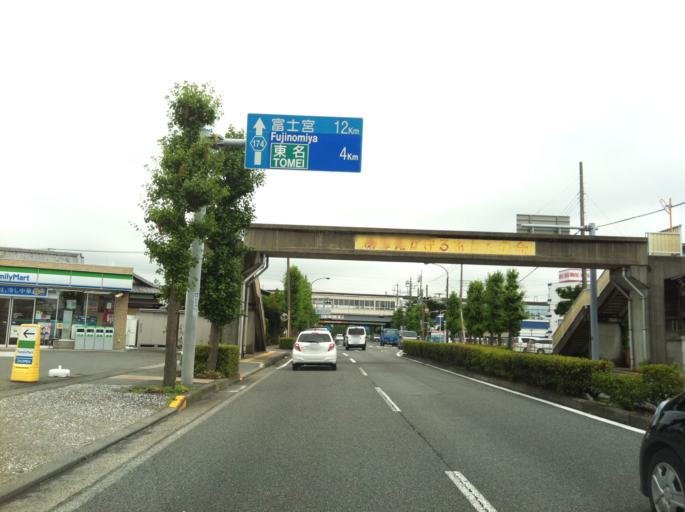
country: JP
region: Shizuoka
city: Fuji
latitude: 35.1404
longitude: 138.6624
